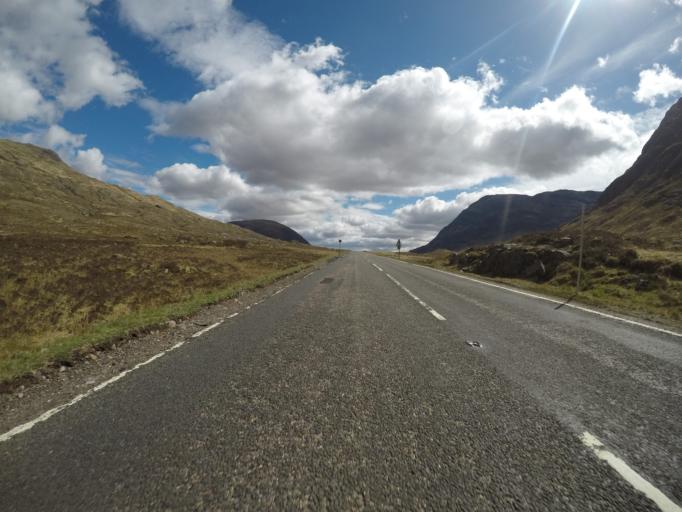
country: GB
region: Scotland
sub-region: Highland
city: Fort William
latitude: 56.6642
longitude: -4.9425
